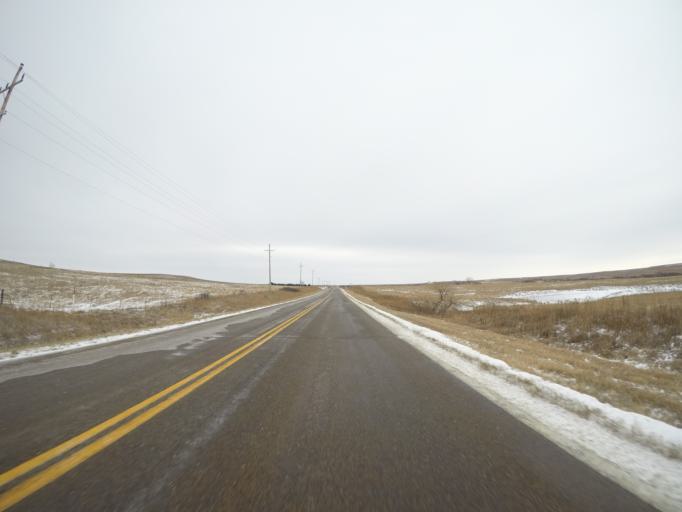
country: US
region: Kansas
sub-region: Wabaunsee County
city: Alma
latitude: 38.8698
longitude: -96.1844
